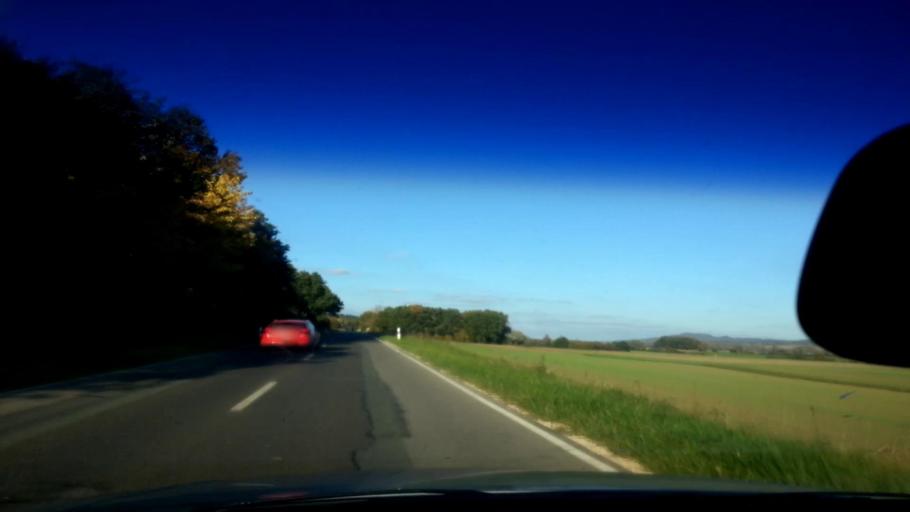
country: DE
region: Bavaria
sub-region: Upper Franconia
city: Rattelsdorf
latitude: 50.0283
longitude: 10.9095
